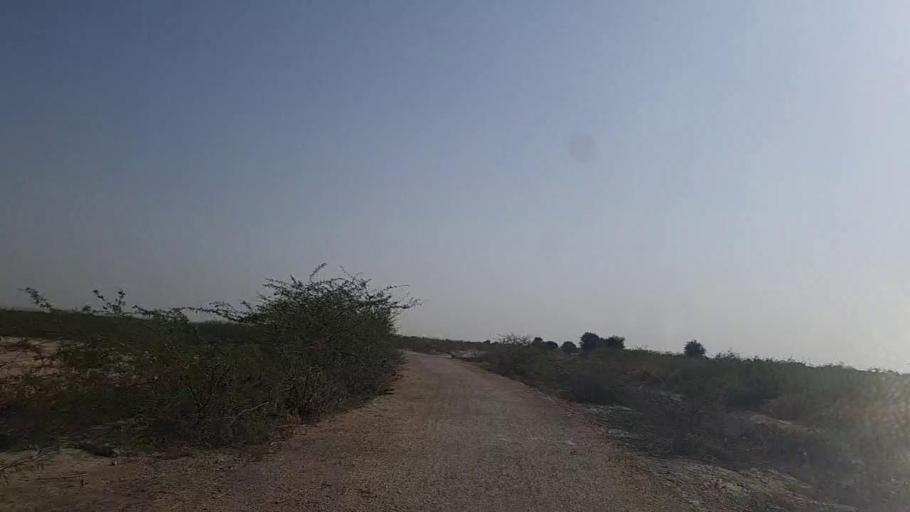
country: PK
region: Sindh
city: Kadhan
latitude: 24.5936
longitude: 69.2628
